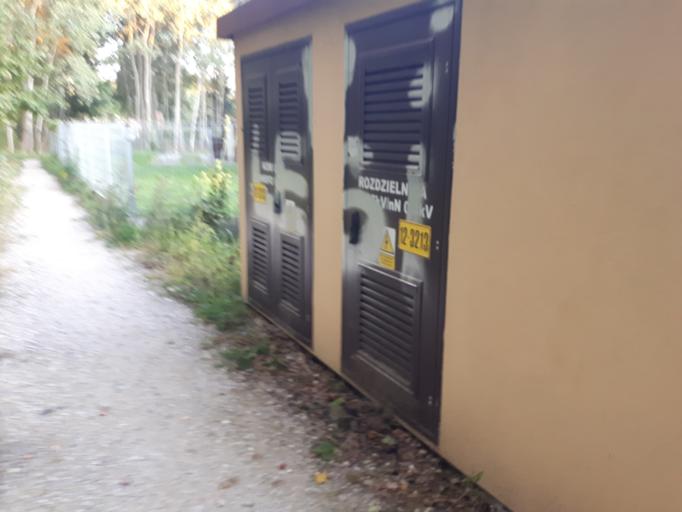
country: PL
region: Masovian Voivodeship
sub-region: Powiat wolominski
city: Kobylka
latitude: 52.3457
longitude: 21.1746
